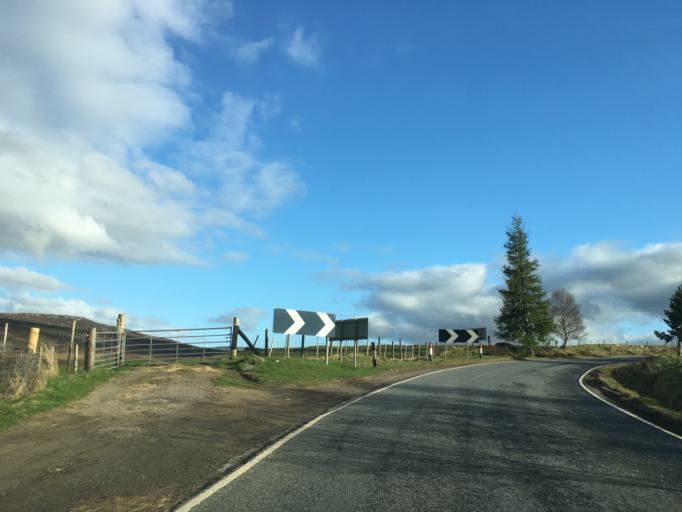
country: GB
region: Scotland
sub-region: Highland
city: Kingussie
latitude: 57.0032
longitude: -4.2461
